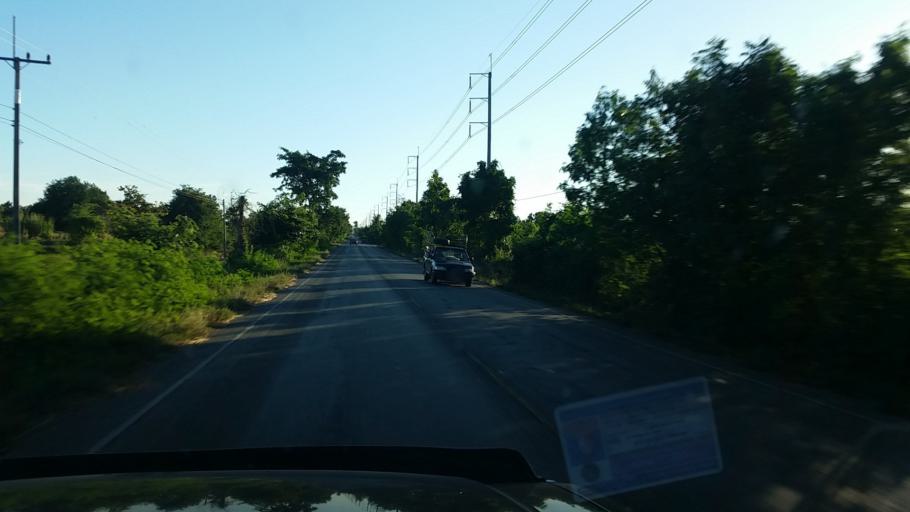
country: TH
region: Chaiyaphum
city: Nong Bua Rawe
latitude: 15.7034
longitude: 101.7368
